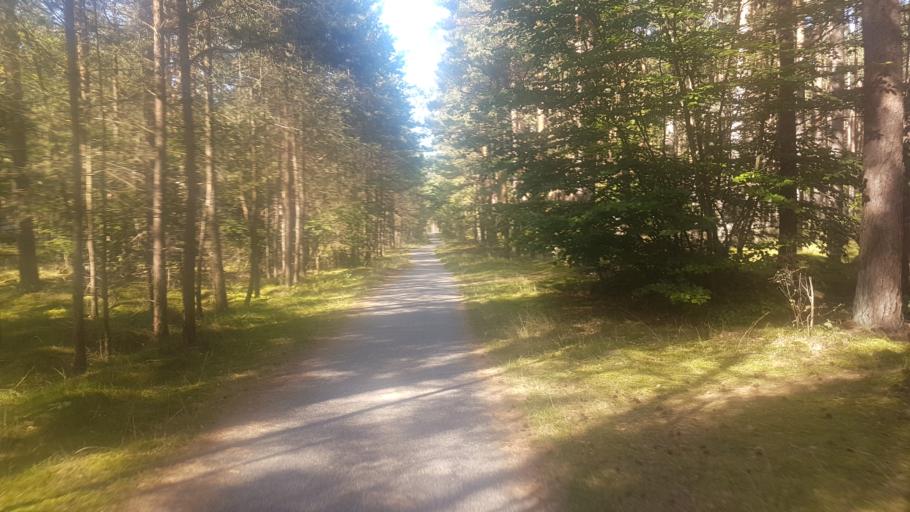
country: DE
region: Mecklenburg-Vorpommern
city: Glowe
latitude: 54.5762
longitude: 13.4171
